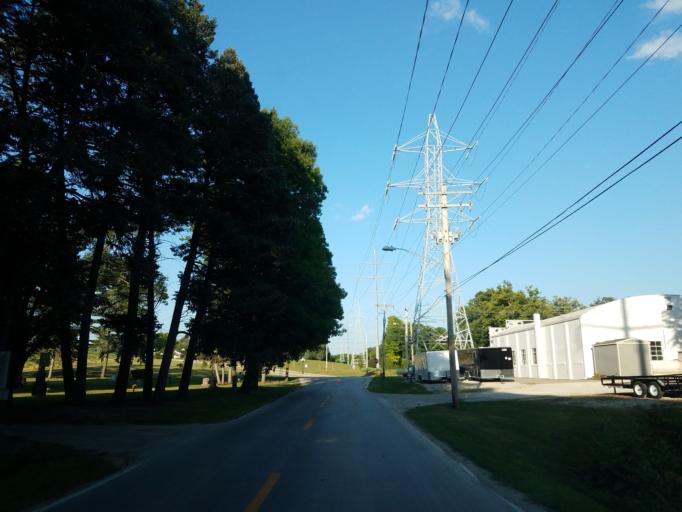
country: US
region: Illinois
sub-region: McLean County
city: Bloomington
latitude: 40.4643
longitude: -89.0073
